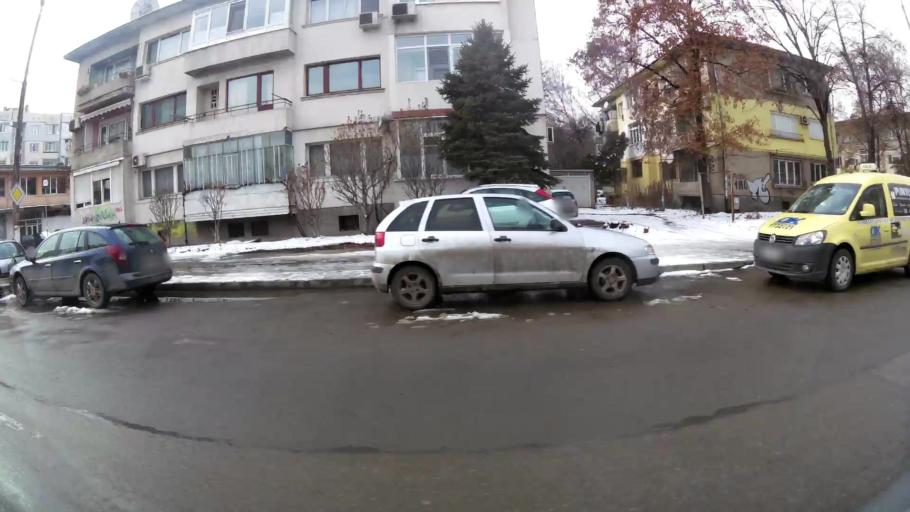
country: BG
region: Sofia-Capital
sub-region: Stolichna Obshtina
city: Sofia
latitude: 42.7086
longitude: 23.3505
